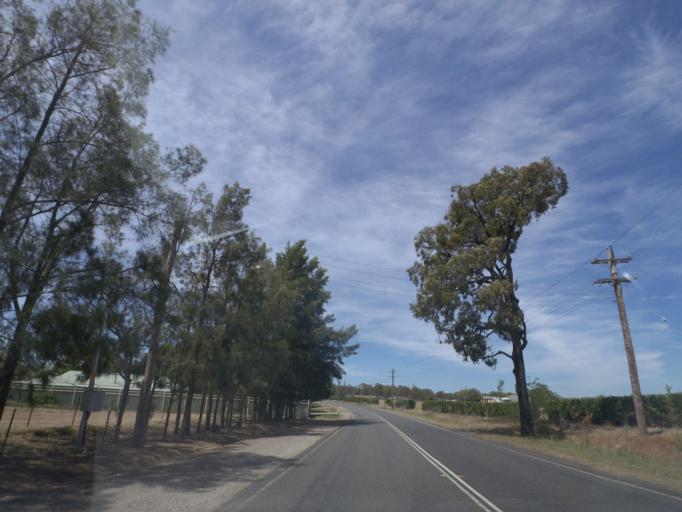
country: AU
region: New South Wales
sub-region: Wollondilly
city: Buxton
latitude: -34.3126
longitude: 150.5881
